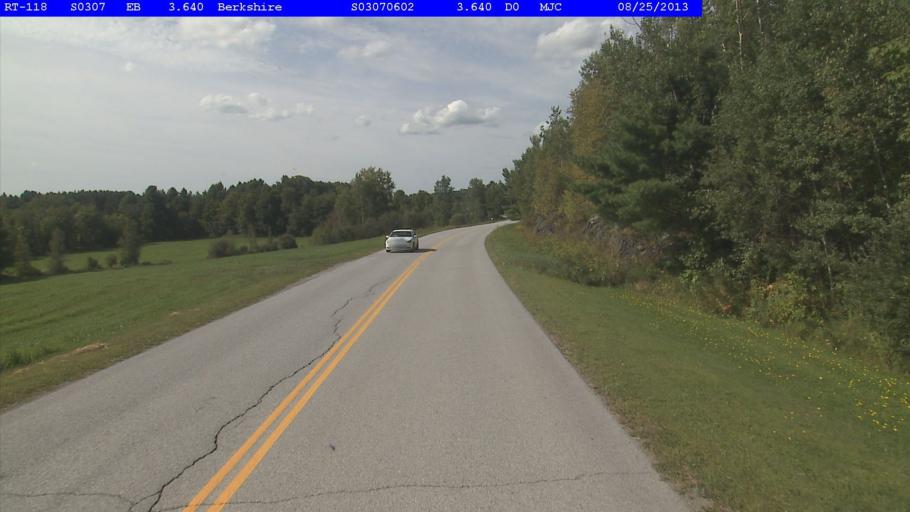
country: US
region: Vermont
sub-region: Franklin County
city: Enosburg Falls
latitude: 44.9676
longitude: -72.7614
